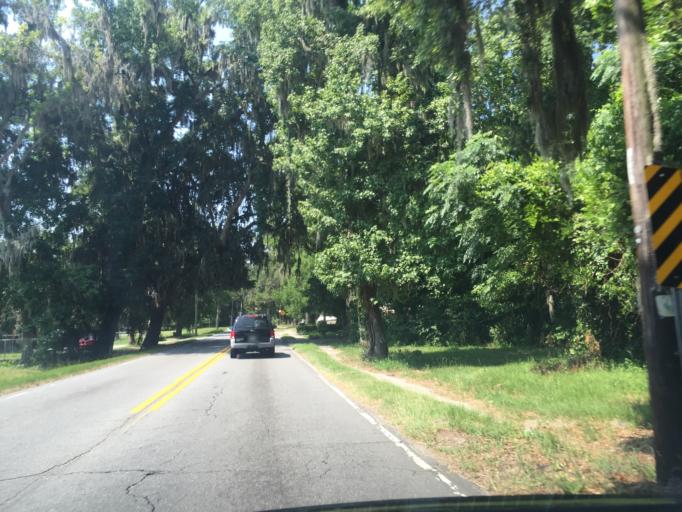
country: US
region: Georgia
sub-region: Chatham County
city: Montgomery
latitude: 31.9698
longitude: -81.1339
